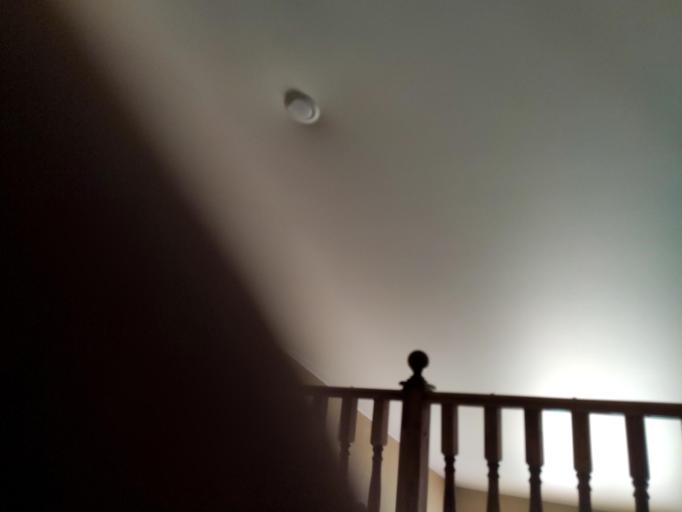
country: RU
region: Krasnodarskiy
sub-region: Sochi City
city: Khosta
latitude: 43.5515
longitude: 39.8004
